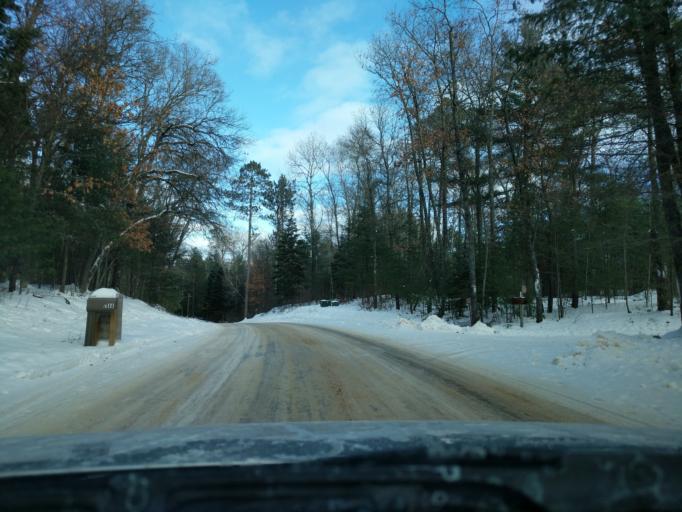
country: US
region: Wisconsin
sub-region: Vilas County
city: Eagle River
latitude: 45.7938
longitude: -89.0772
